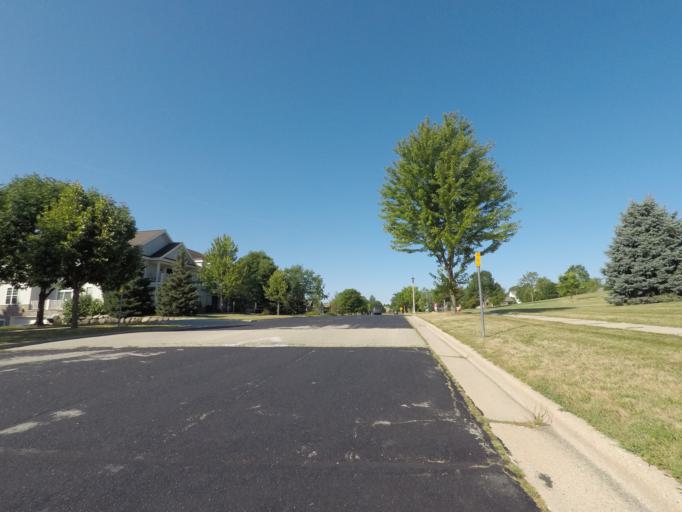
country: US
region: Wisconsin
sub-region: Dane County
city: Shorewood Hills
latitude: 43.0194
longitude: -89.4316
